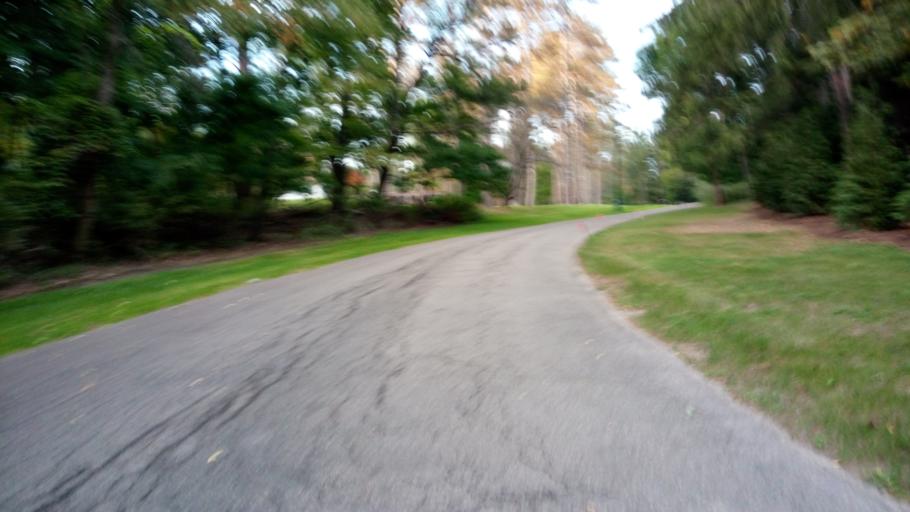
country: US
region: New York
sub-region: Chemung County
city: West Elmira
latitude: 42.0914
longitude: -76.8335
